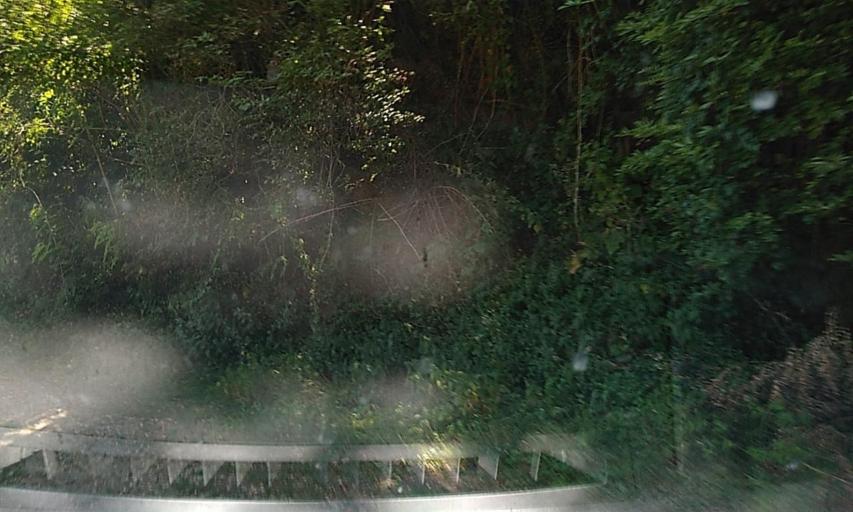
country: RS
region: Central Serbia
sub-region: Pcinjski Okrug
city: Vladicin Han
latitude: 42.7600
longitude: 22.0723
